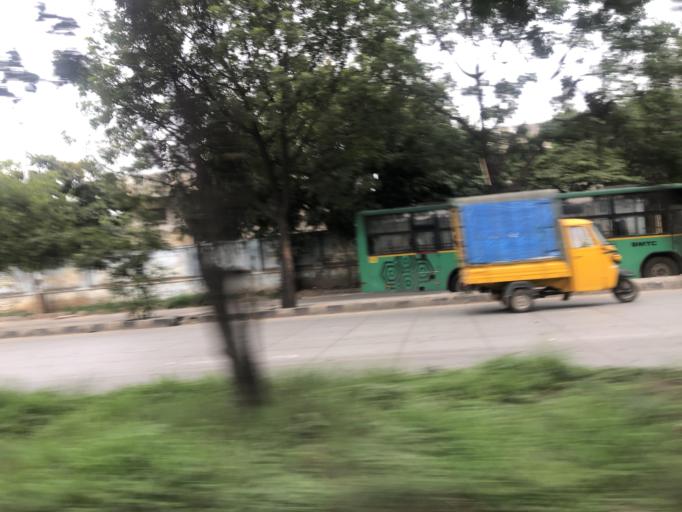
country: IN
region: Karnataka
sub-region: Bangalore Urban
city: Bangalore
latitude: 12.9926
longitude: 77.5212
